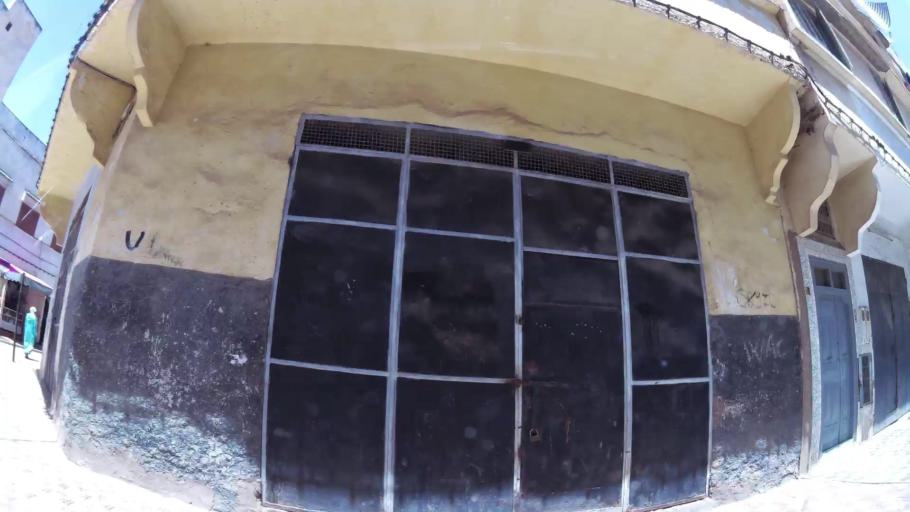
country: MA
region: Rabat-Sale-Zemmour-Zaer
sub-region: Khemisset
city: Khemisset
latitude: 33.8281
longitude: -6.0725
